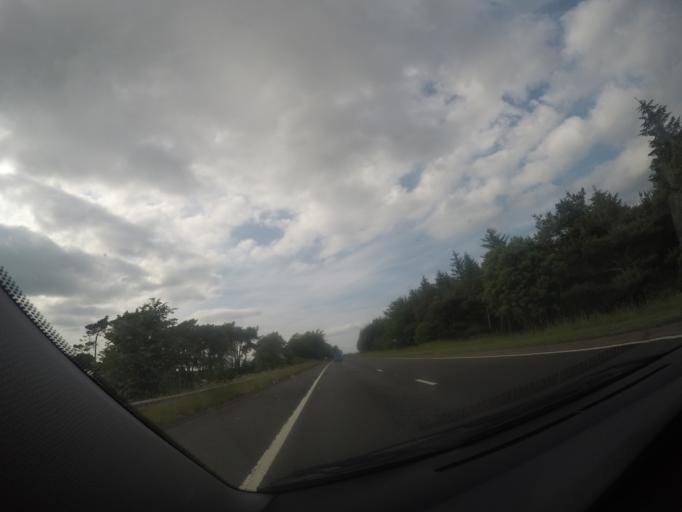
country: GB
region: Scotland
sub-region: South Lanarkshire
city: Blackwood
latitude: 55.6874
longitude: -3.9415
